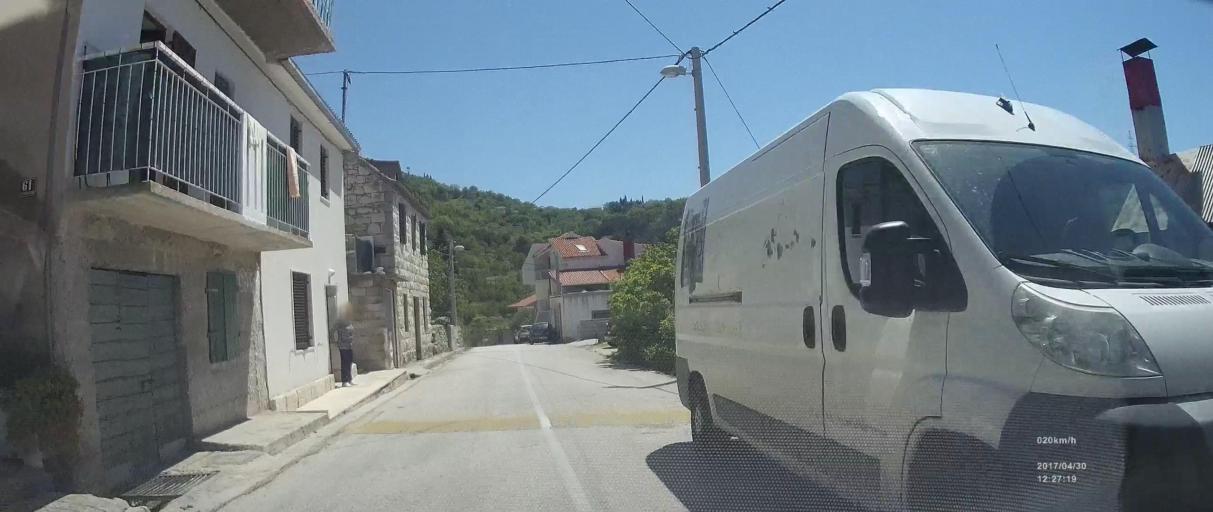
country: HR
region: Splitsko-Dalmatinska
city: Srinjine
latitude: 43.5066
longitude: 16.5967
